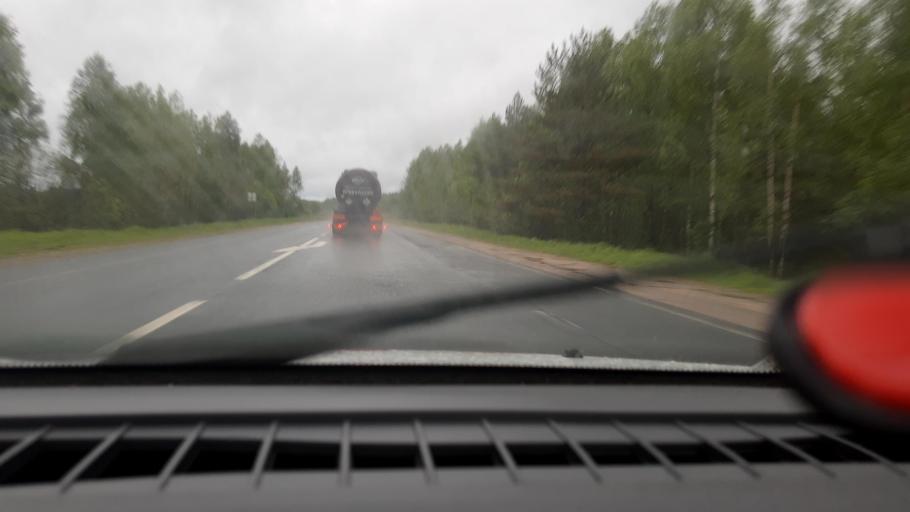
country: RU
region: Nizjnij Novgorod
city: Sukhobezvodnoye
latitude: 56.8611
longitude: 44.8549
